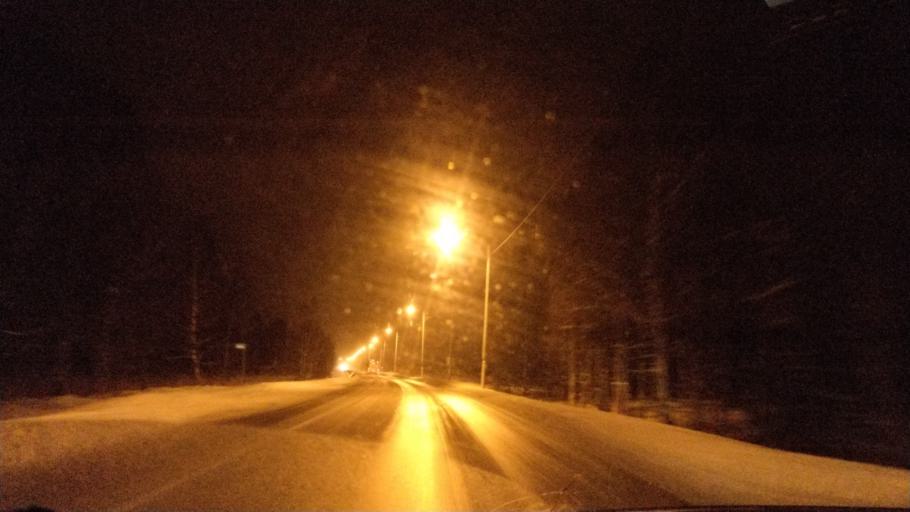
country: FI
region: Lapland
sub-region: Rovaniemi
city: Rovaniemi
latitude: 66.2854
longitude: 25.3411
